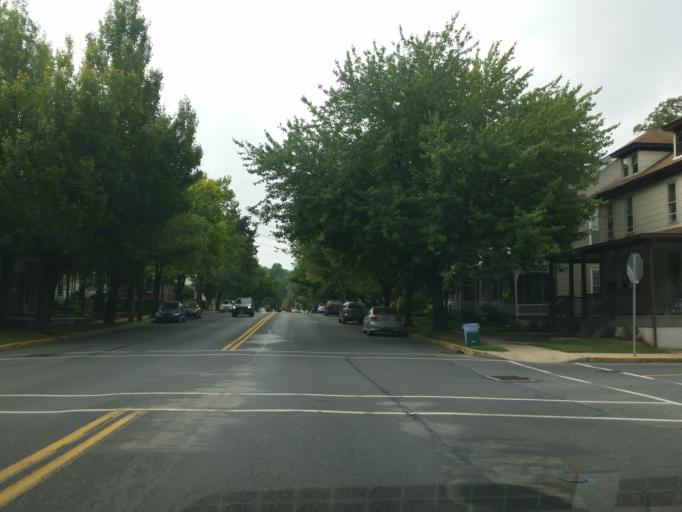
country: US
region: Pennsylvania
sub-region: Lancaster County
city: Lititz
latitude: 40.1533
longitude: -76.3072
